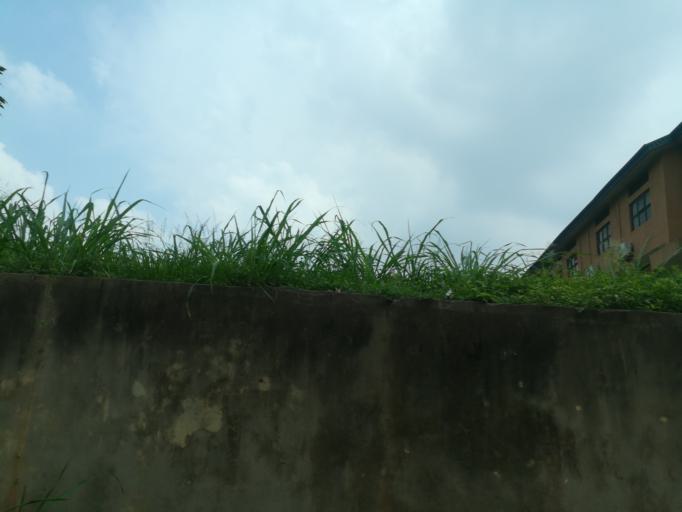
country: NG
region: Oyo
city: Ibadan
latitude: 7.4100
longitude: 3.9043
